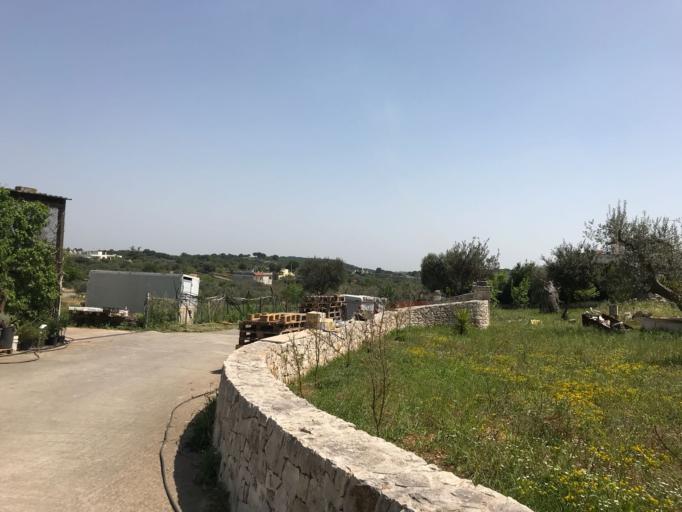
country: IT
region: Apulia
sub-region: Provincia di Brindisi
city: Casalini
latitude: 40.7396
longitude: 17.4751
